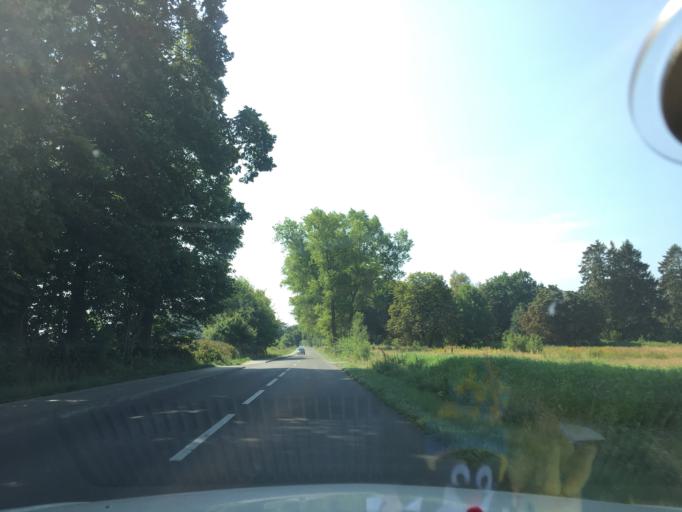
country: PL
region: West Pomeranian Voivodeship
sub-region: Powiat gryficki
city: Pobierowo
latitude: 54.0305
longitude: 14.8743
